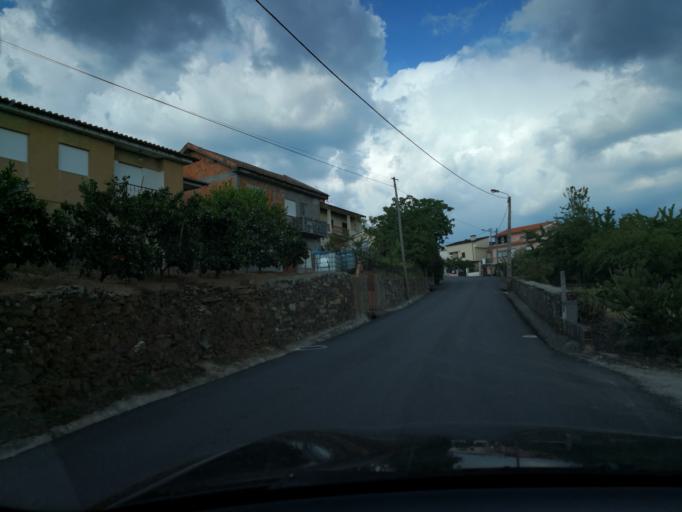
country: PT
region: Vila Real
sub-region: Sabrosa
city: Vilela
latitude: 41.2238
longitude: -7.6905
